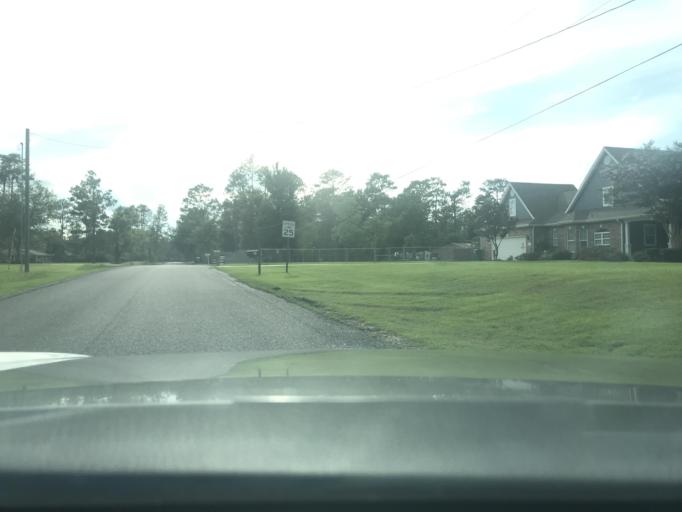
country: US
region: Louisiana
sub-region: Calcasieu Parish
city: Moss Bluff
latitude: 30.3371
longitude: -93.2581
